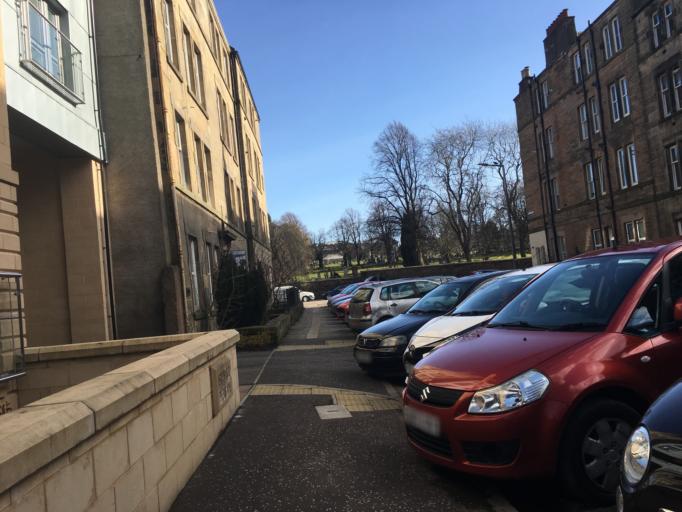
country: GB
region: Scotland
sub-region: Edinburgh
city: Edinburgh
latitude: 55.9256
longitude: -3.2150
